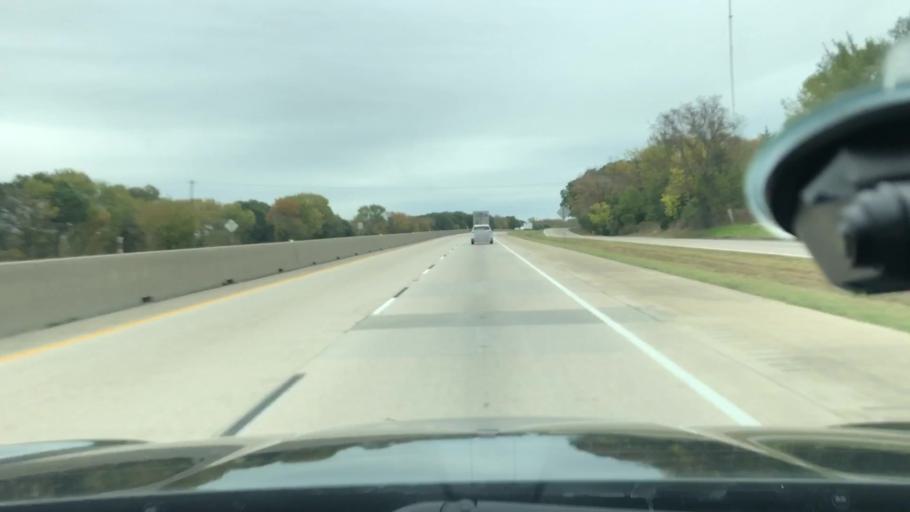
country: US
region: Texas
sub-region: Hopkins County
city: Sulphur Springs
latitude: 33.1269
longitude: -95.7469
